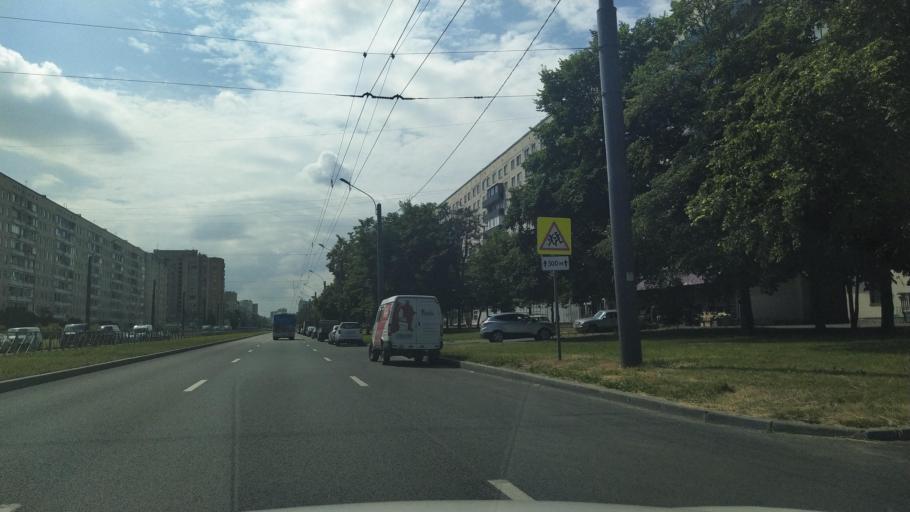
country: RU
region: Leningrad
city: Parnas
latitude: 60.0521
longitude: 30.3566
